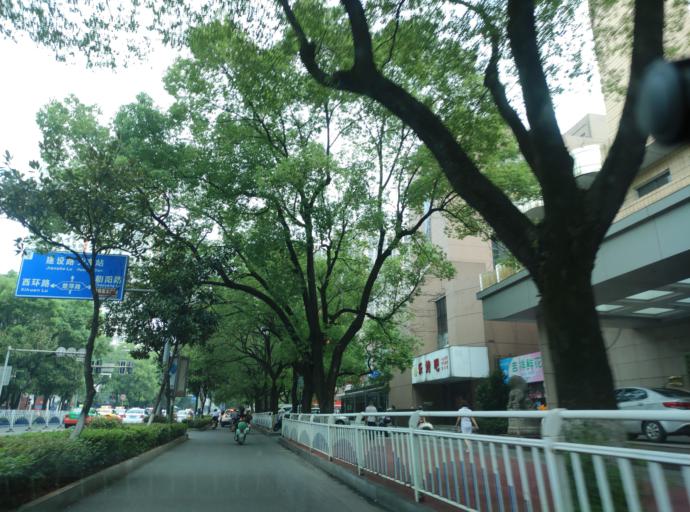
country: CN
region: Jiangxi Sheng
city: Pingxiang
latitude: 27.6433
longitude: 113.8404
